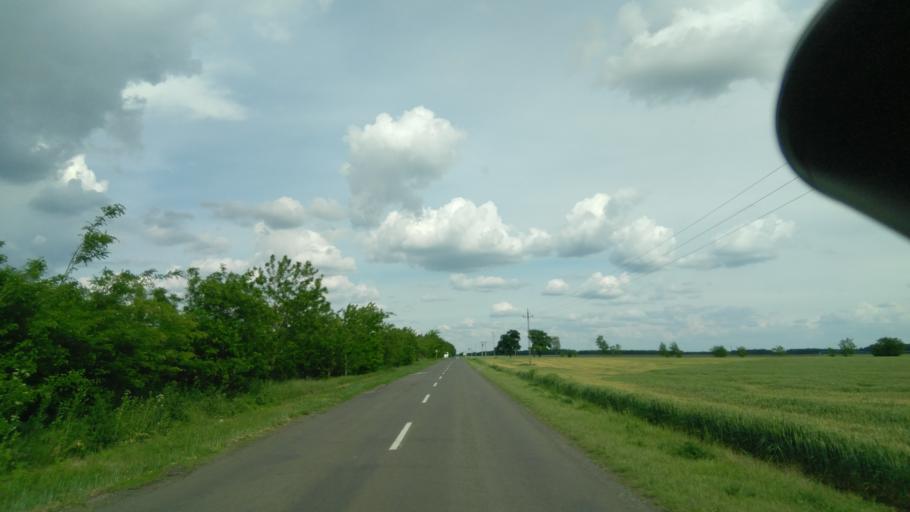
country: RO
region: Arad
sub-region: Comuna Peregu Mare
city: Peregu Mare
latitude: 46.3053
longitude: 20.9008
